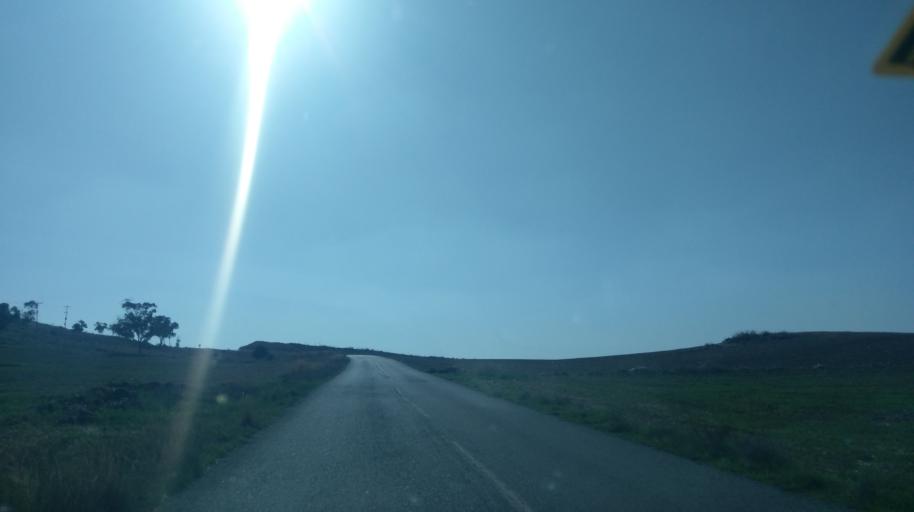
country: CY
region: Larnaka
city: Athienou
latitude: 35.0666
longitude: 33.4828
